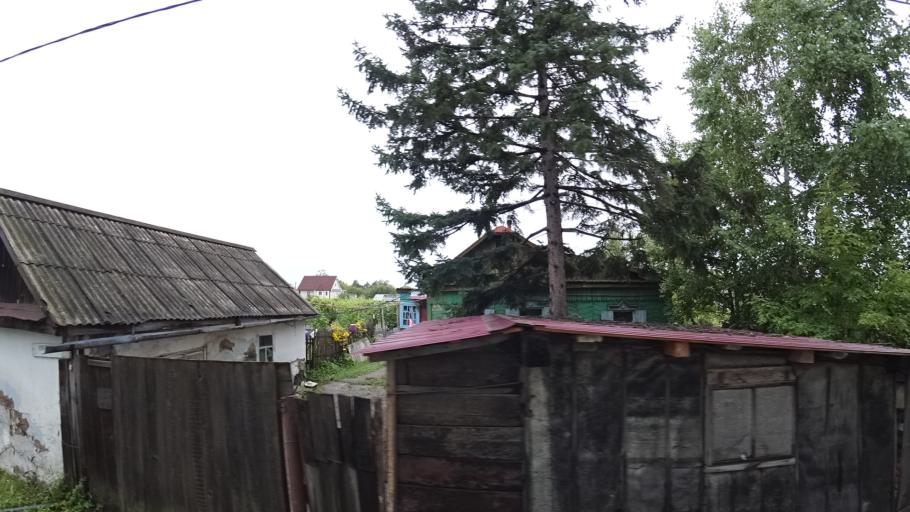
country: RU
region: Primorskiy
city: Monastyrishche
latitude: 44.2103
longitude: 132.4332
